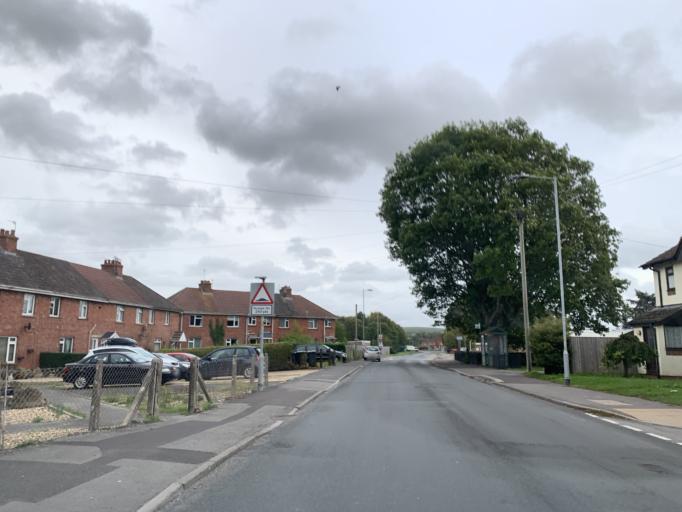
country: GB
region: England
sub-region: Wiltshire
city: Boreham
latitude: 51.2031
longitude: -2.1654
